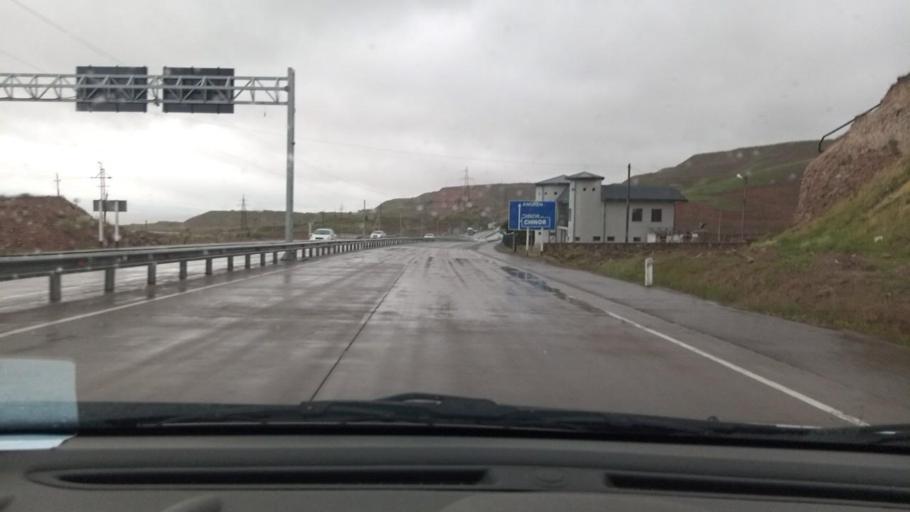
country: UZ
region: Toshkent
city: Angren
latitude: 41.0626
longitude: 70.2110
